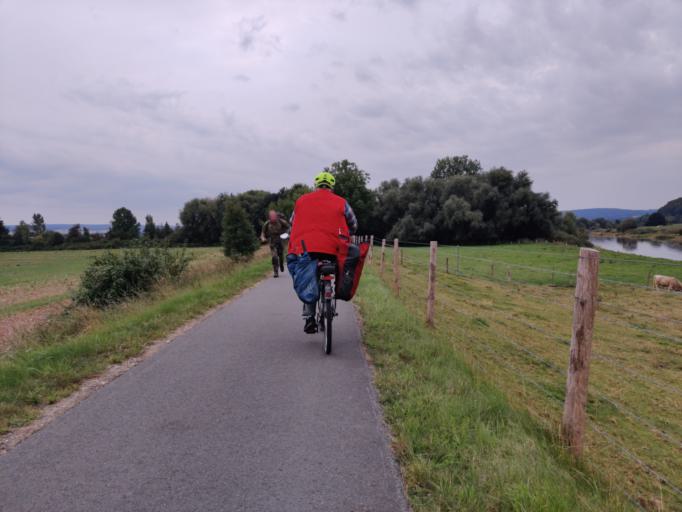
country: DE
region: Lower Saxony
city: Holzminden
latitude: 51.8553
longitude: 9.4618
